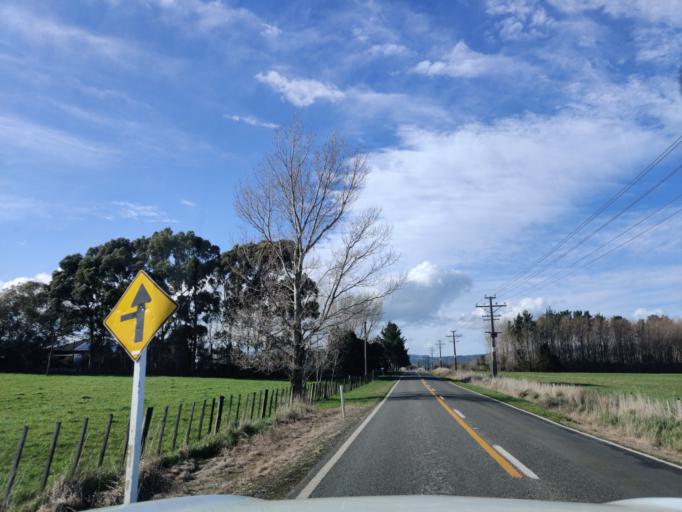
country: NZ
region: Manawatu-Wanganui
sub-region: Palmerston North City
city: Palmerston North
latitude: -40.3399
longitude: 175.7194
